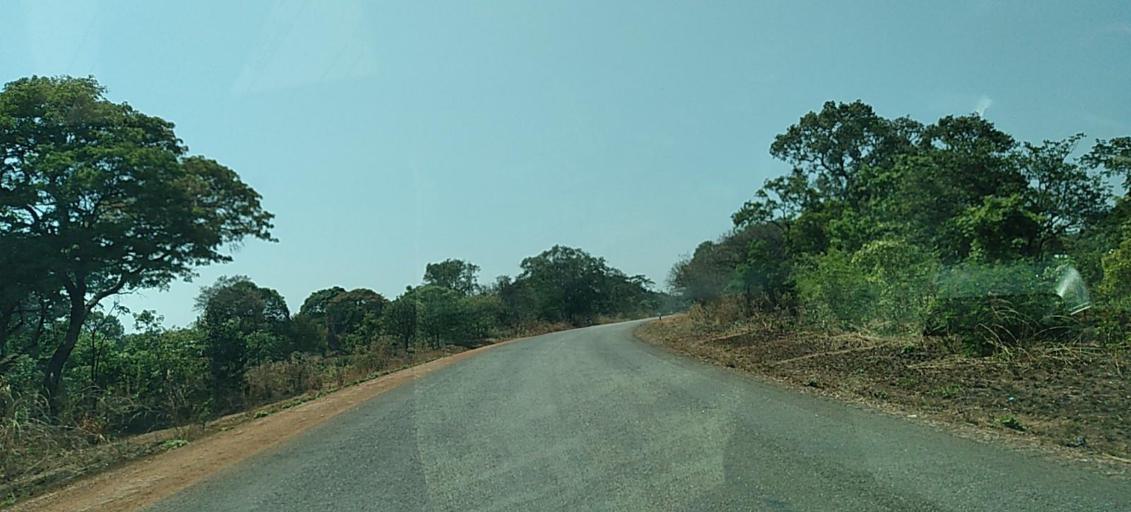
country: ZM
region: North-Western
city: Solwezi
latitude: -12.2759
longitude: 25.6787
